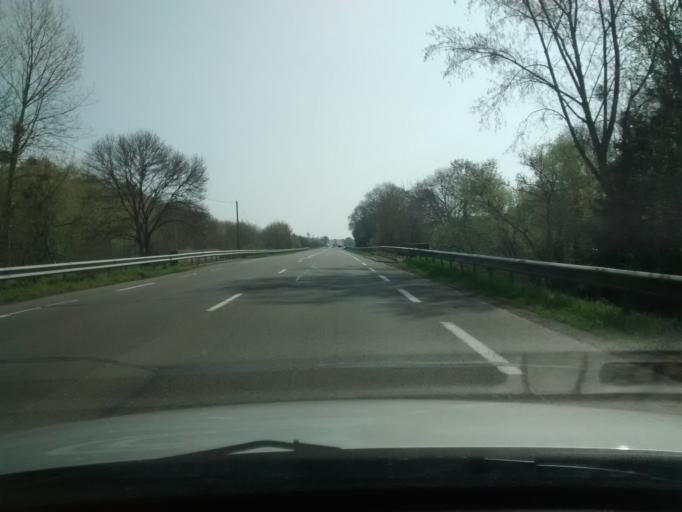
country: FR
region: Pays de la Loire
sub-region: Departement de la Mayenne
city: Argentre
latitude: 48.0673
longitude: -0.6603
